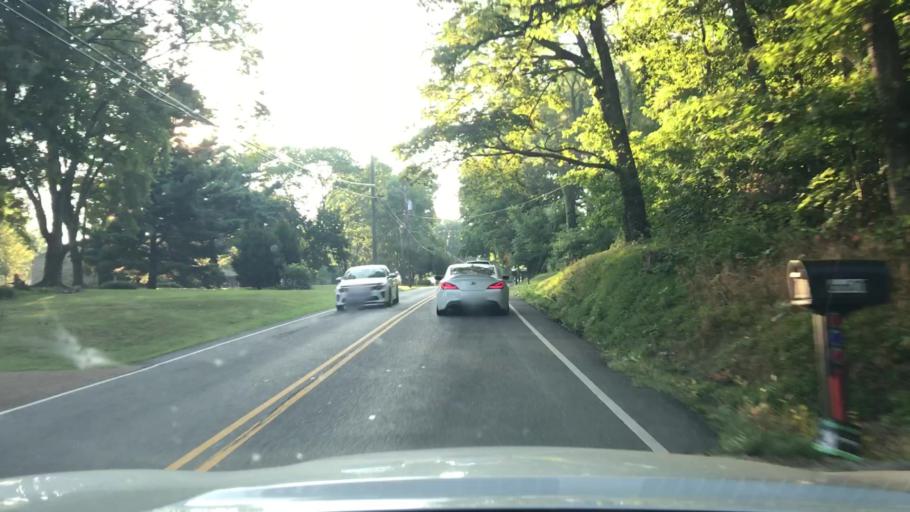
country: US
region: Tennessee
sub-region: Williamson County
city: Nolensville
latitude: 35.9908
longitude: -86.6425
